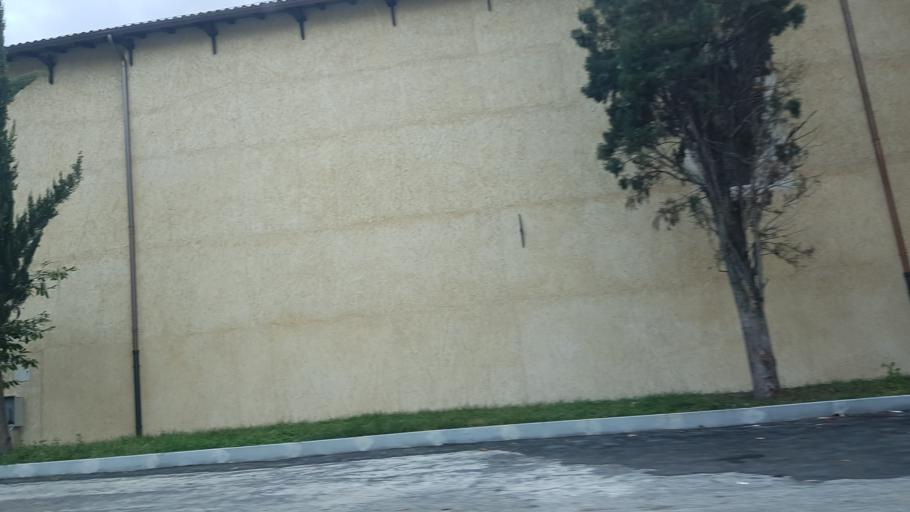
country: IT
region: Abruzzo
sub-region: Provincia dell' Aquila
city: L'Aquila
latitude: 42.3522
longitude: 13.4135
